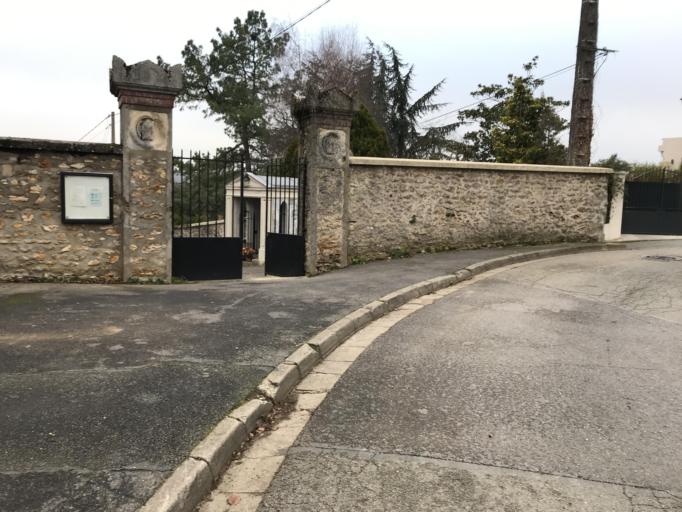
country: FR
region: Ile-de-France
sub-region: Departement de l'Essonne
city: Bievres
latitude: 48.7566
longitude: 2.2147
